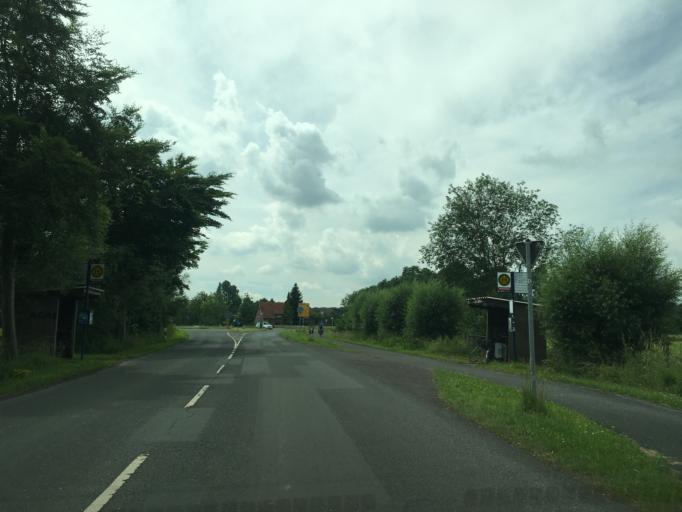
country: DE
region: North Rhine-Westphalia
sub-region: Regierungsbezirk Munster
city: Havixbeck
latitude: 51.9944
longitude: 7.4542
